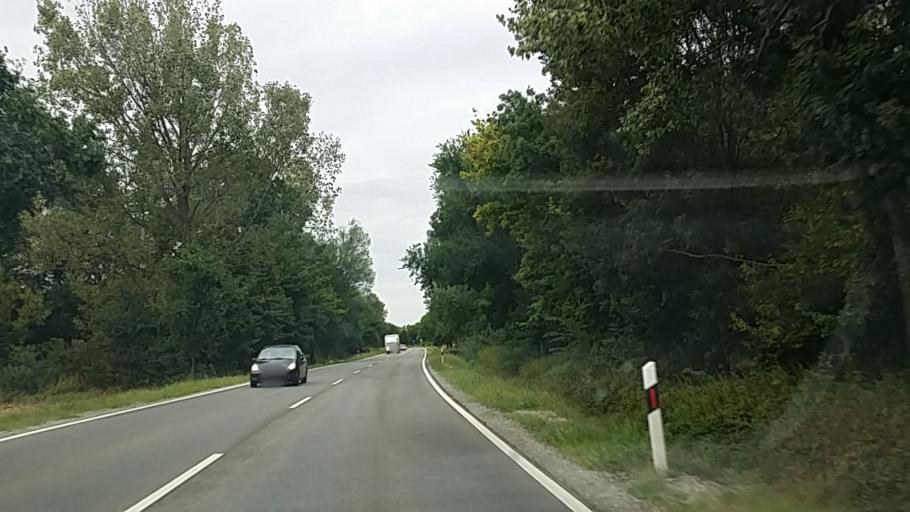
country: HU
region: Gyor-Moson-Sopron
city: Fertoszentmiklos
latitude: 47.5946
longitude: 16.8368
